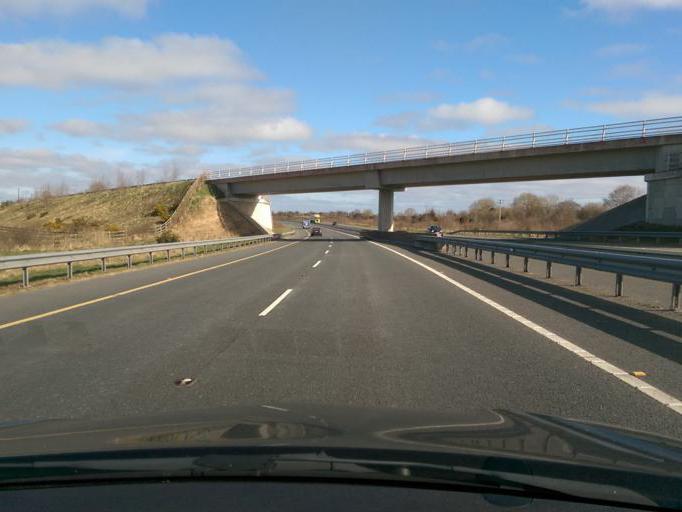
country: IE
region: Leinster
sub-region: An Iarmhi
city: Athlone
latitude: 53.3535
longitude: -8.0657
